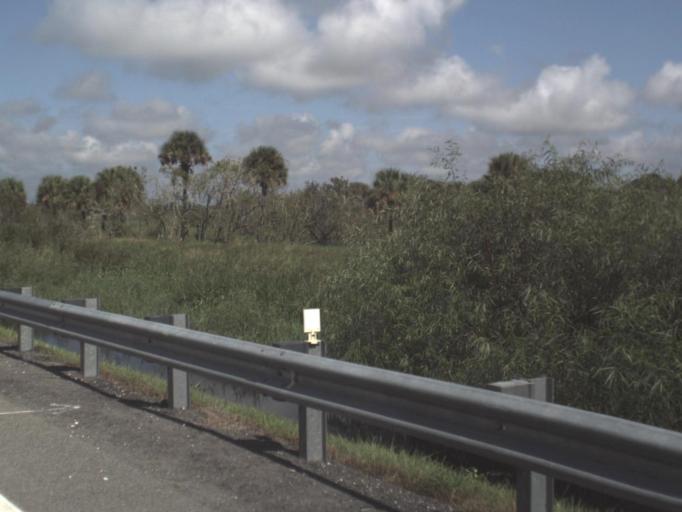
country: US
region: Florida
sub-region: Sarasota County
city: Lake Sarasota
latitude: 27.2326
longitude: -82.3090
